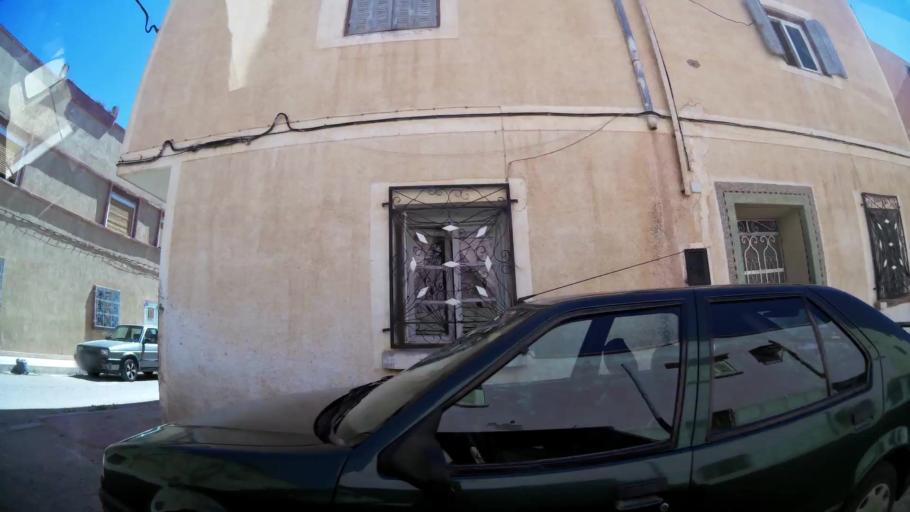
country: MA
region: Oriental
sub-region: Oujda-Angad
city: Oujda
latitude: 34.6666
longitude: -1.8722
